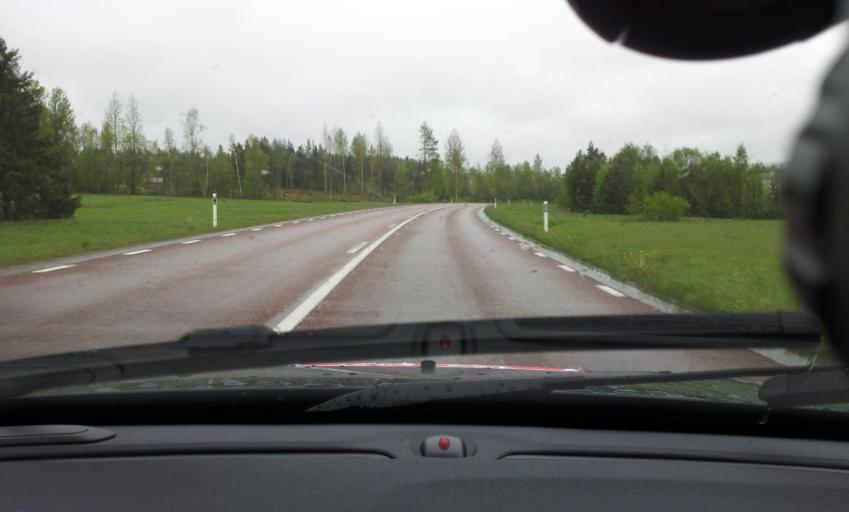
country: SE
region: Jaemtland
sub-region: Bergs Kommun
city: Hoverberg
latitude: 62.7594
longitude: 14.4378
